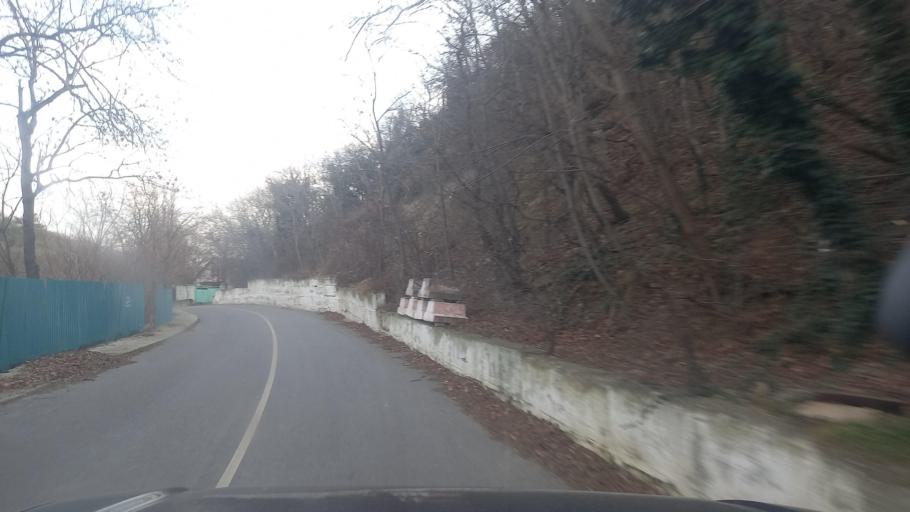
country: RU
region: Krasnodarskiy
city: Myskhako
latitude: 44.6600
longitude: 37.6849
